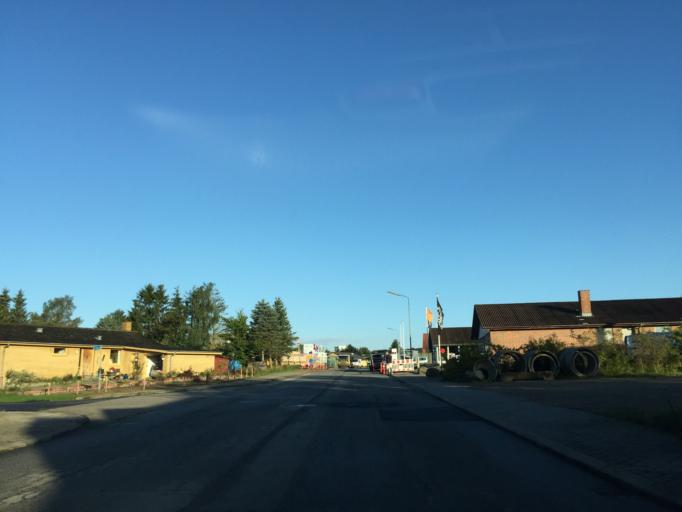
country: DK
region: Central Jutland
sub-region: Viborg Kommune
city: Bjerringbro
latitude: 56.3782
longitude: 9.6742
